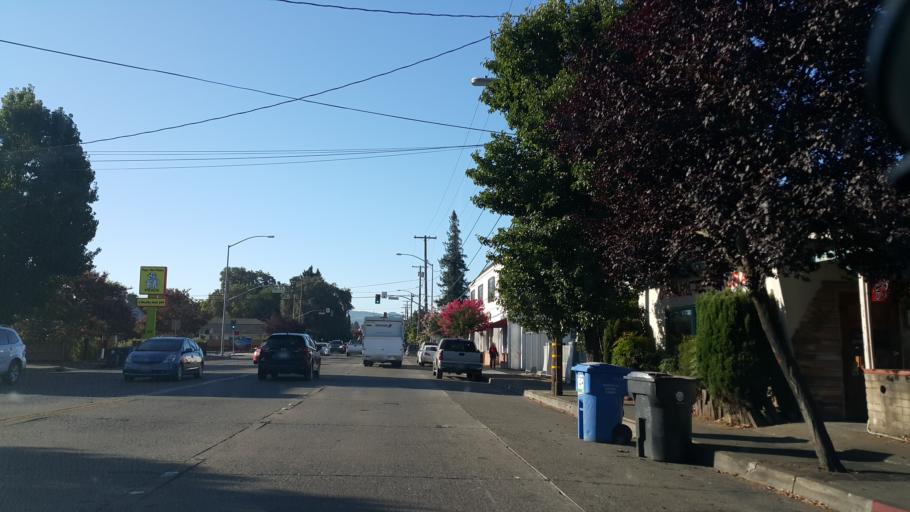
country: US
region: California
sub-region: Mendocino County
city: Ukiah
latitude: 39.1548
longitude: -123.2083
